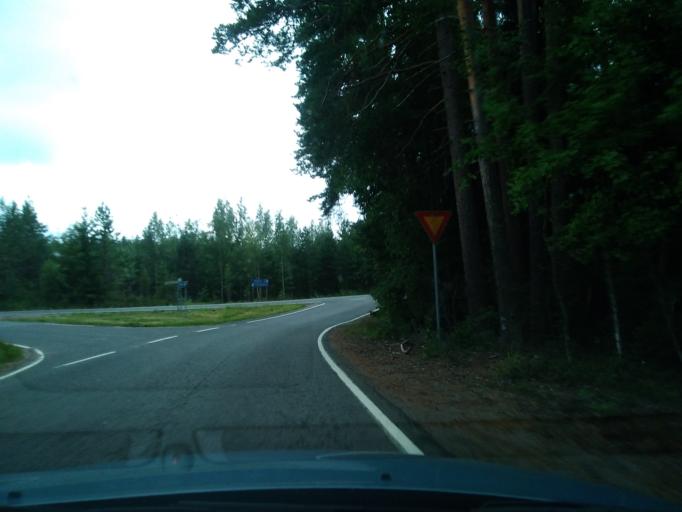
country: FI
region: Uusimaa
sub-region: Helsinki
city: Kaerkoelae
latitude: 60.7714
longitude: 24.0730
